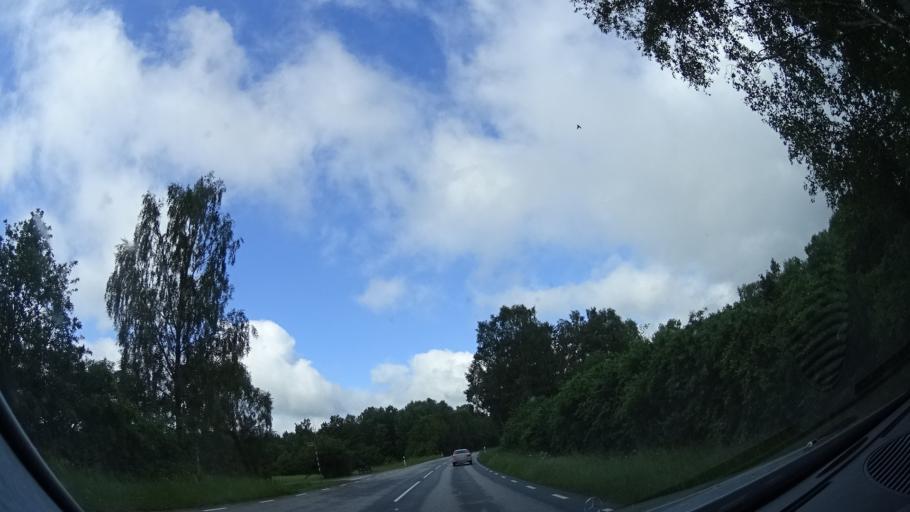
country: SE
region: Skane
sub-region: Eslovs Kommun
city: Stehag
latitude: 55.9432
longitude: 13.4177
